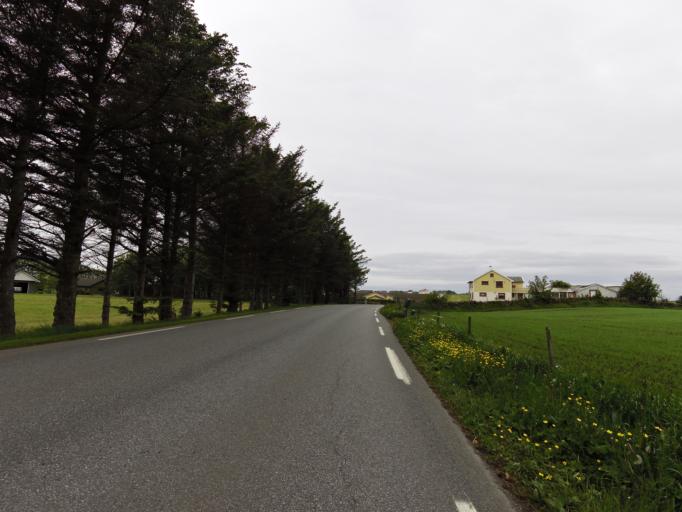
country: NO
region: Rogaland
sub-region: Klepp
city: Kleppe
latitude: 58.8144
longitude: 5.5801
